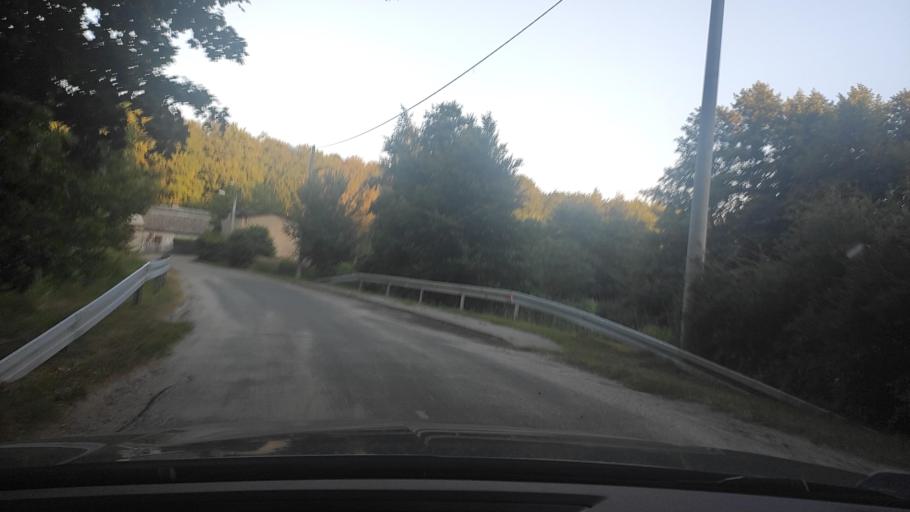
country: PL
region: Greater Poland Voivodeship
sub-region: Powiat poznanski
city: Kobylnica
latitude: 52.4469
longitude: 17.1272
